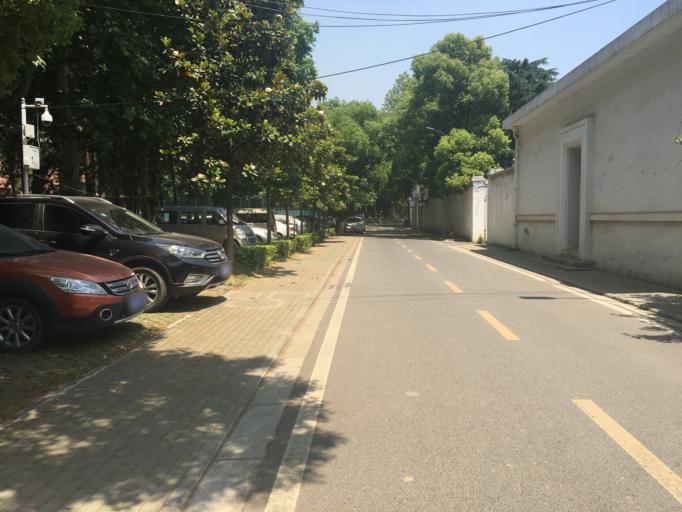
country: CN
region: Hubei
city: Guanshan
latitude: 30.5294
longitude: 114.3574
